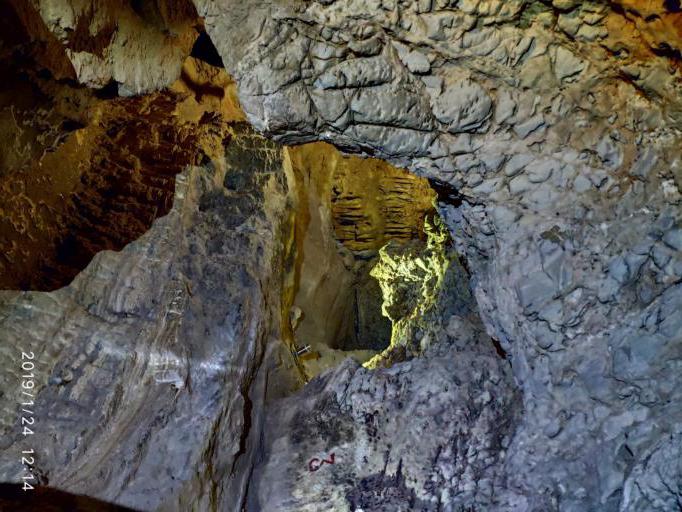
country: ES
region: Andalusia
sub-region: Provincia de Malaga
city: Nerja
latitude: 36.7619
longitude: -3.8448
